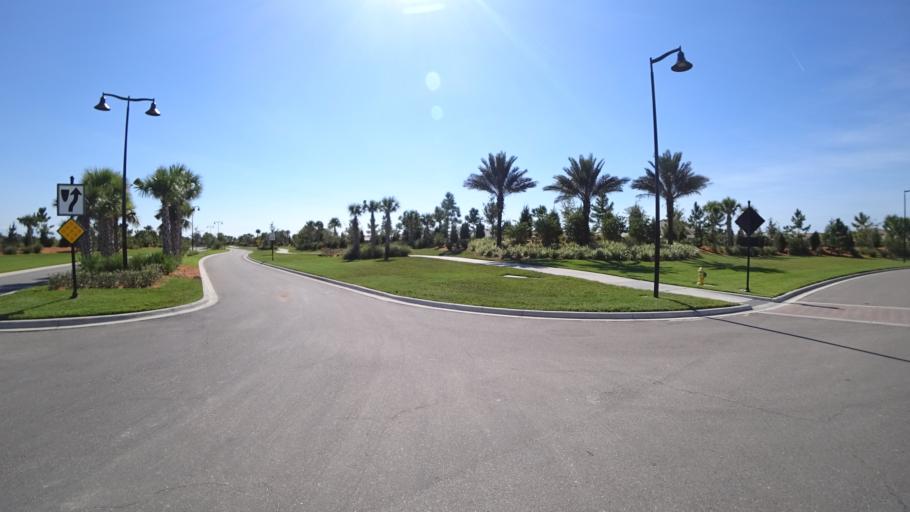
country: US
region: Florida
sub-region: Sarasota County
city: The Meadows
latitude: 27.4105
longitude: -82.3612
